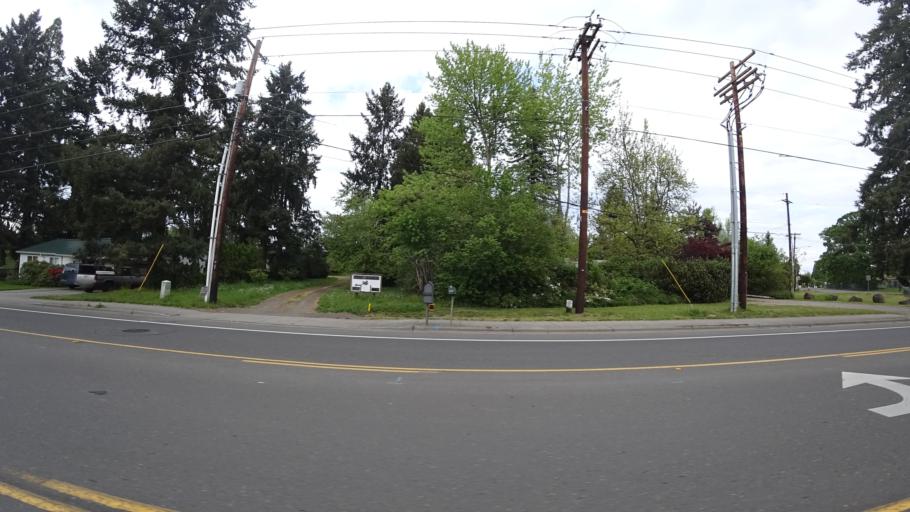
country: US
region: Oregon
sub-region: Washington County
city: Hillsboro
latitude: 45.4972
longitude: -122.9459
